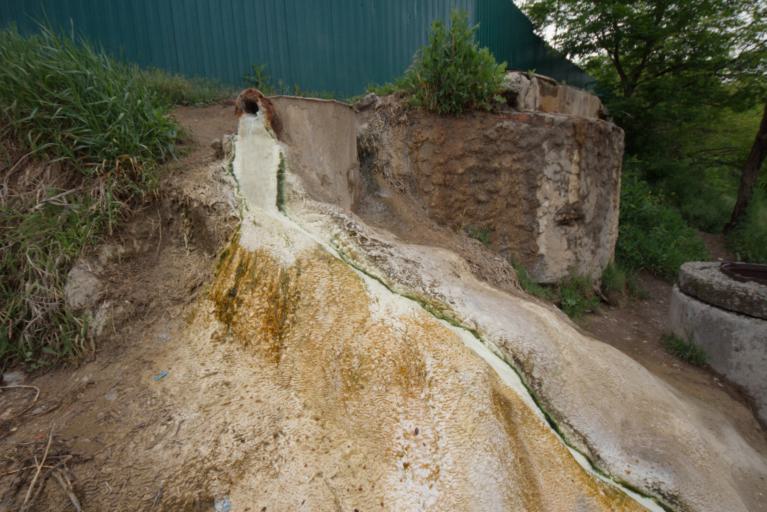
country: RU
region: Stavropol'skiy
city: Goryachevodskiy
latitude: 44.0402
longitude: 43.0934
